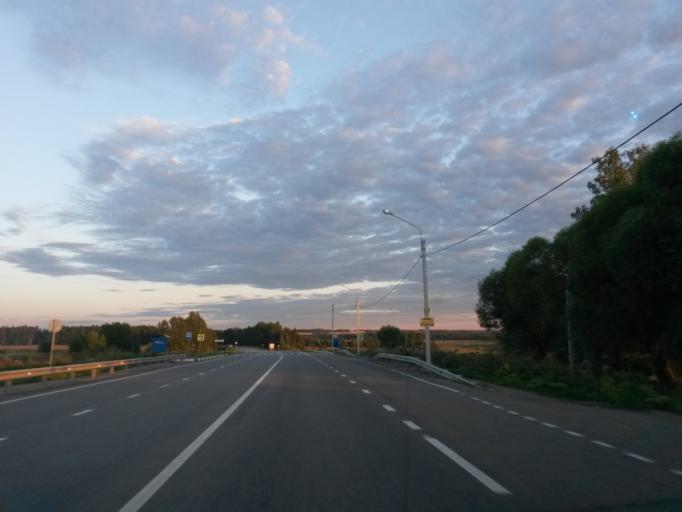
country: RU
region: Jaroslavl
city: Gavrilov-Yam
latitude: 57.3476
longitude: 39.9095
